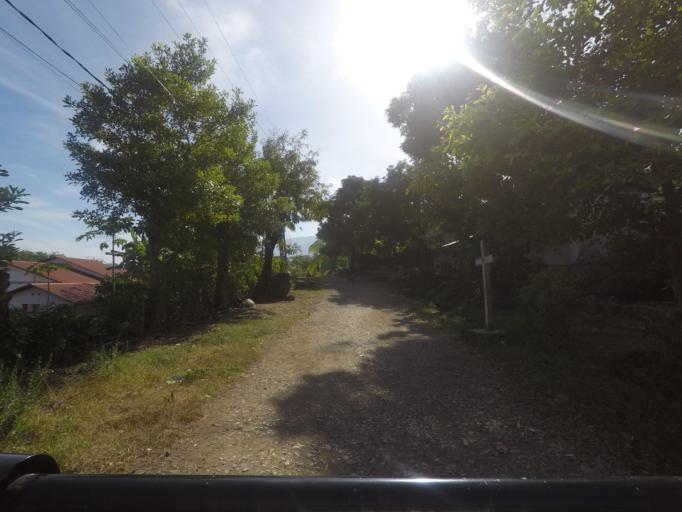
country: TL
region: Bobonaro
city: Maliana
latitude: -8.9972
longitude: 125.2246
